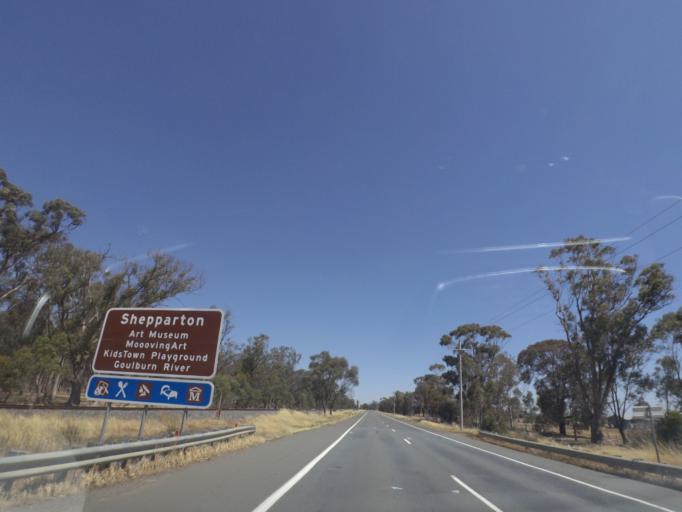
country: AU
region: Victoria
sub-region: Greater Shepparton
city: Shepparton
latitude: -36.2273
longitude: 145.4318
